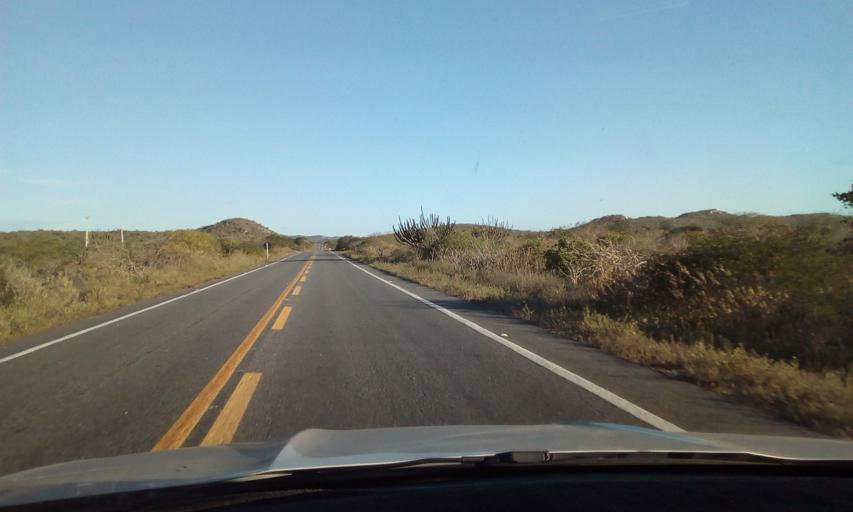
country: BR
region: Paraiba
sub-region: Areia
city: Remigio
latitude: -6.8718
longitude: -35.9240
